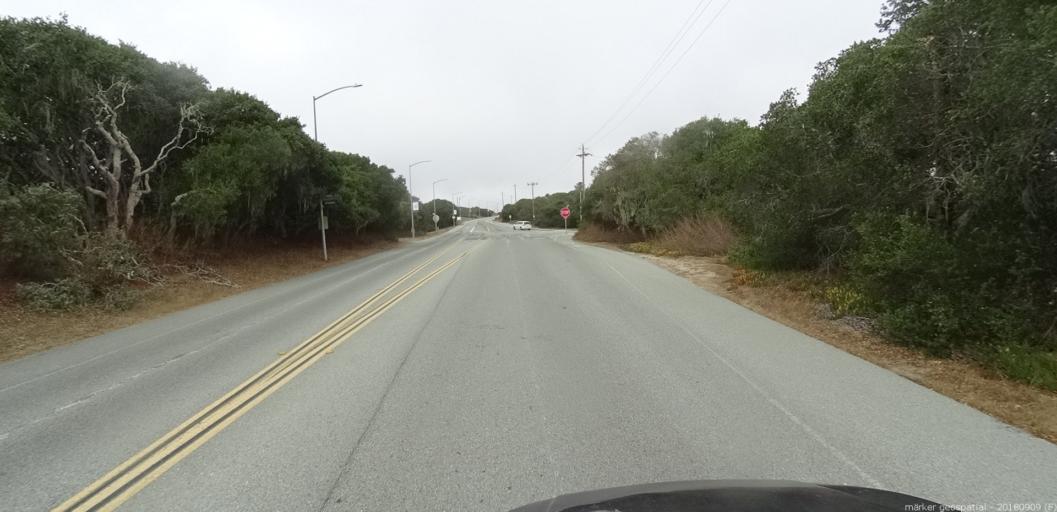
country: US
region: California
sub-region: Monterey County
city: Marina
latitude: 36.6552
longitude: -121.7655
